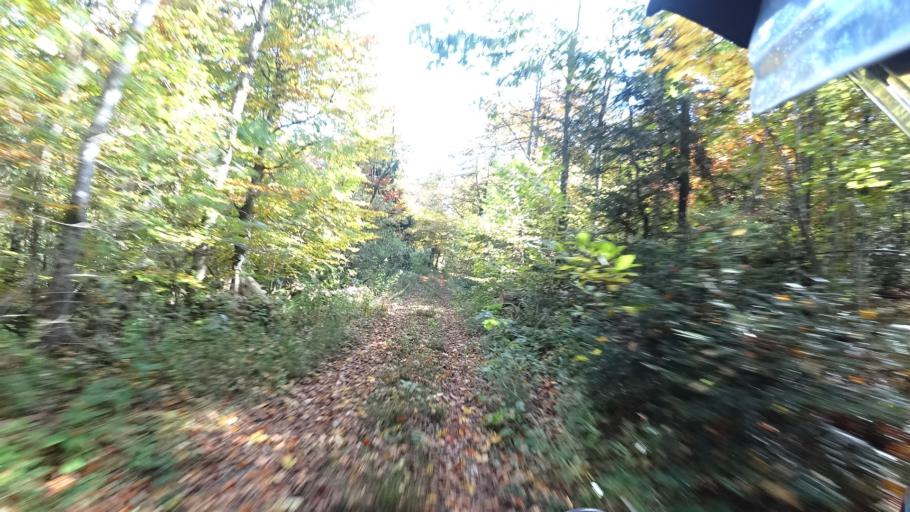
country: HR
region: Karlovacka
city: Plaski
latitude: 45.0714
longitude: 15.3245
